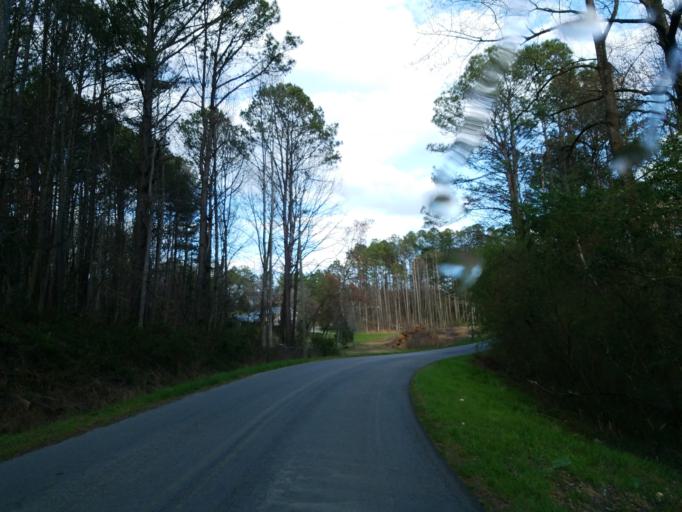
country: US
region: Georgia
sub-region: Bartow County
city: Rydal
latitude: 34.4797
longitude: -84.6705
